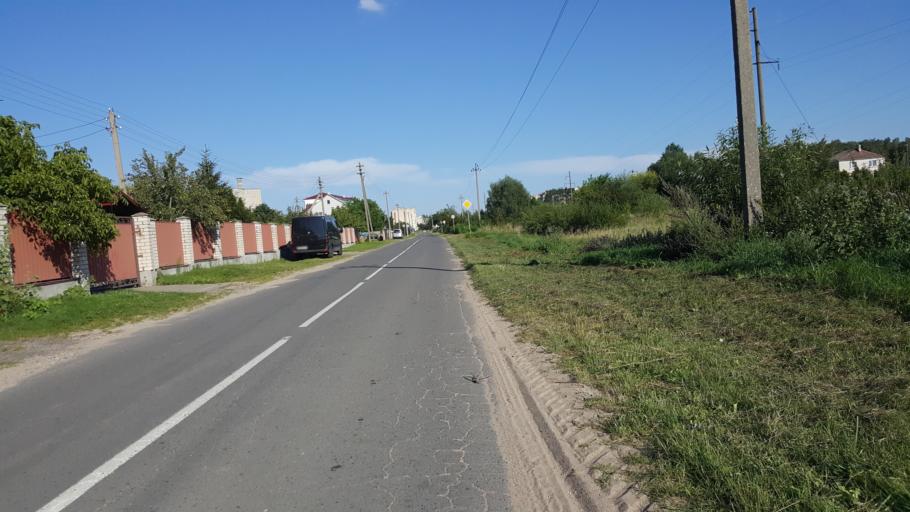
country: BY
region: Brest
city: Kamyanyets
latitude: 52.3940
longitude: 23.8155
